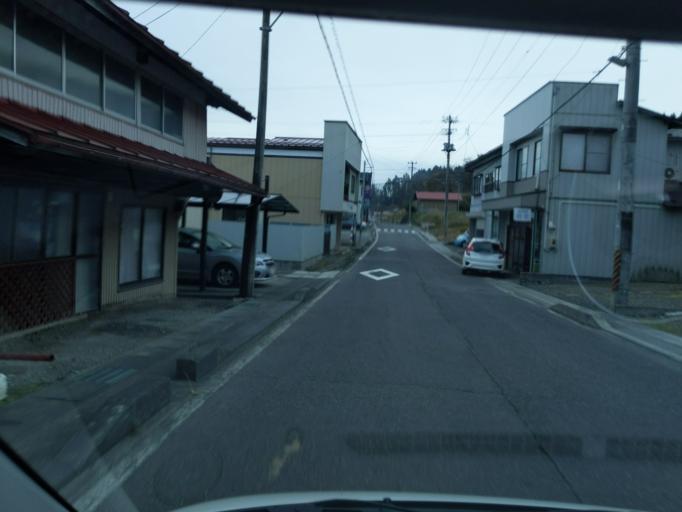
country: JP
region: Iwate
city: Kitakami
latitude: 39.2874
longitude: 141.2622
